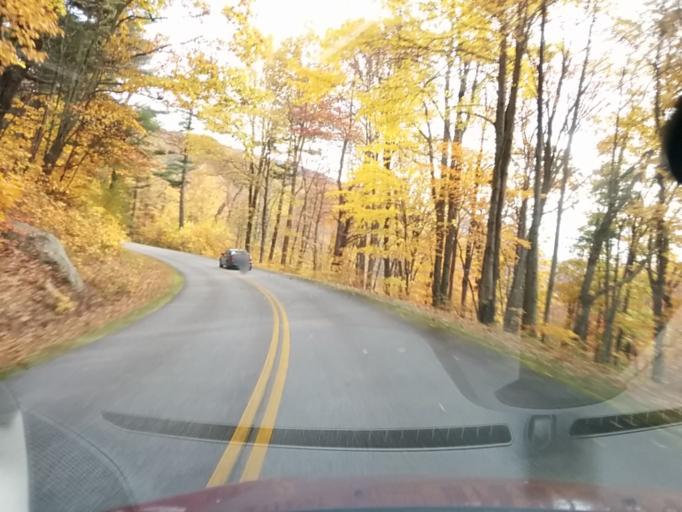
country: US
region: Virginia
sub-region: City of Buena Vista
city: Buena Vista
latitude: 37.8430
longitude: -79.1589
